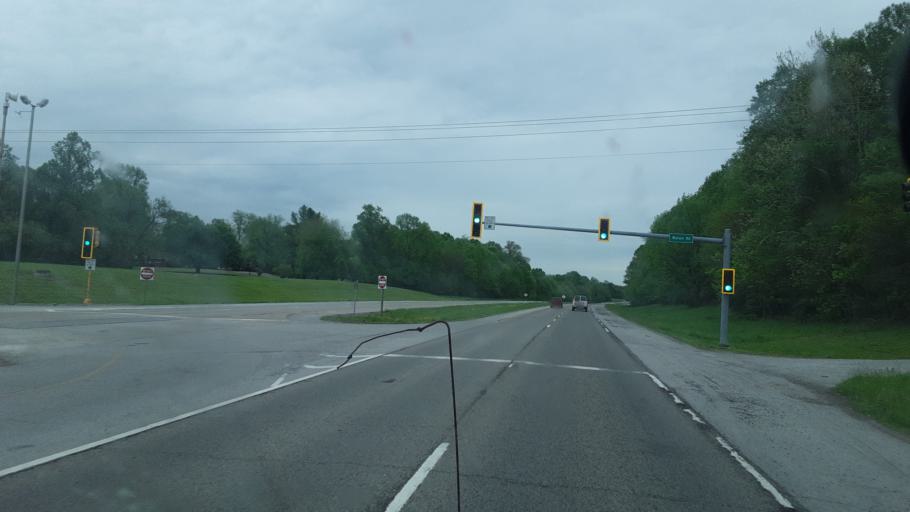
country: US
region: Illinois
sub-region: Jackson County
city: Murphysboro
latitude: 37.7657
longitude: -89.2978
